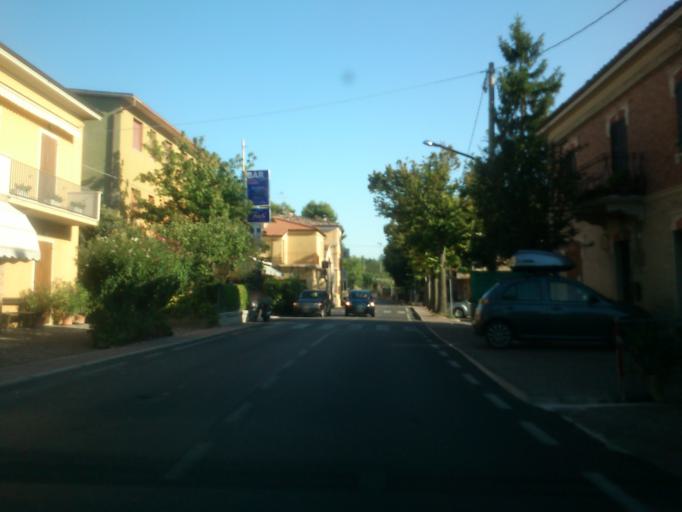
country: IT
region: The Marches
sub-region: Provincia di Pesaro e Urbino
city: Mombaroccio
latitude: 43.8022
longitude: 12.8659
